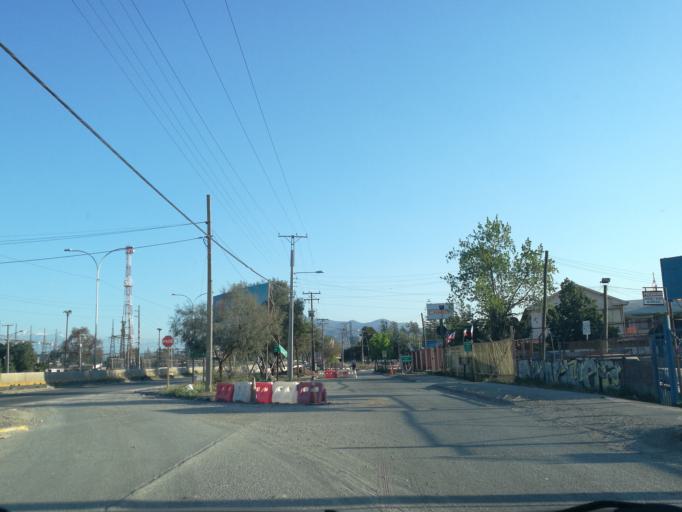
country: CL
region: O'Higgins
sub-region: Provincia de Cachapoal
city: Rancagua
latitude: -34.1640
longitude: -70.7276
